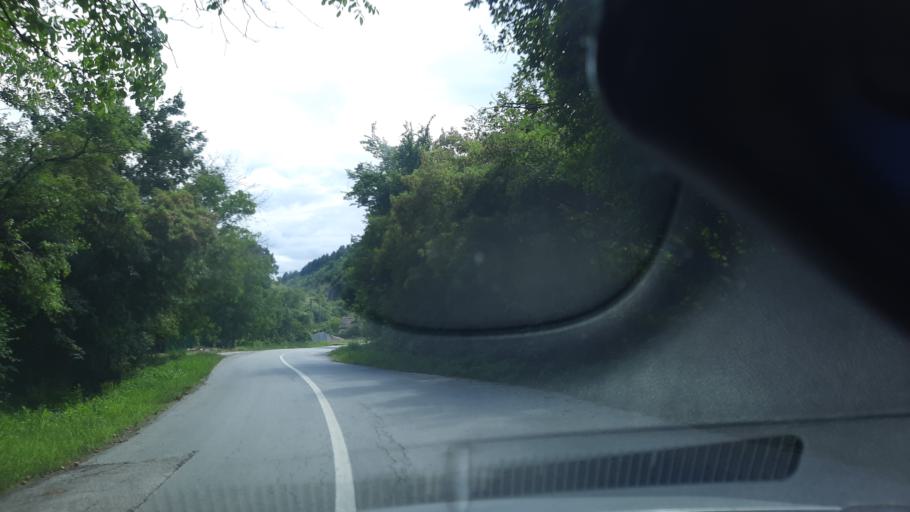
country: RS
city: Celarevo
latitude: 45.1331
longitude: 19.5765
